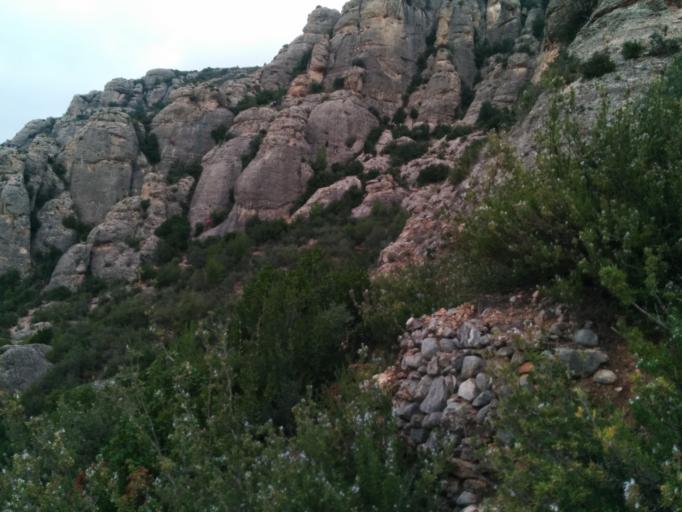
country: ES
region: Catalonia
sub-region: Provincia de Barcelona
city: Collbato
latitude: 41.5749
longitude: 1.8248
